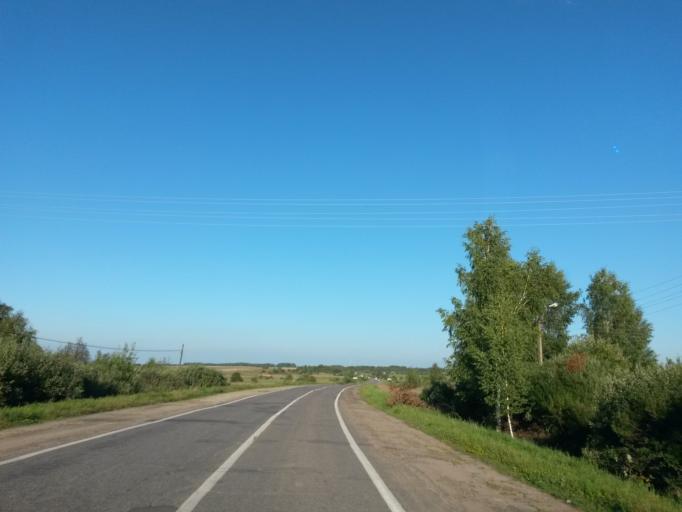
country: RU
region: Jaroslavl
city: Gavrilov-Yam
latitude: 57.3082
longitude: 39.8746
